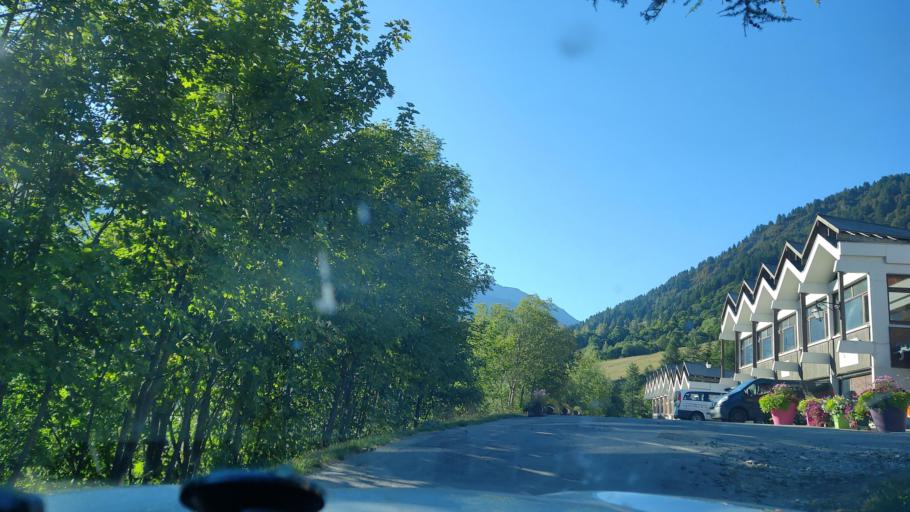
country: FR
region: Rhone-Alpes
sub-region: Departement de la Savoie
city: Saint-Michel-de-Maurienne
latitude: 45.1845
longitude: 6.4720
